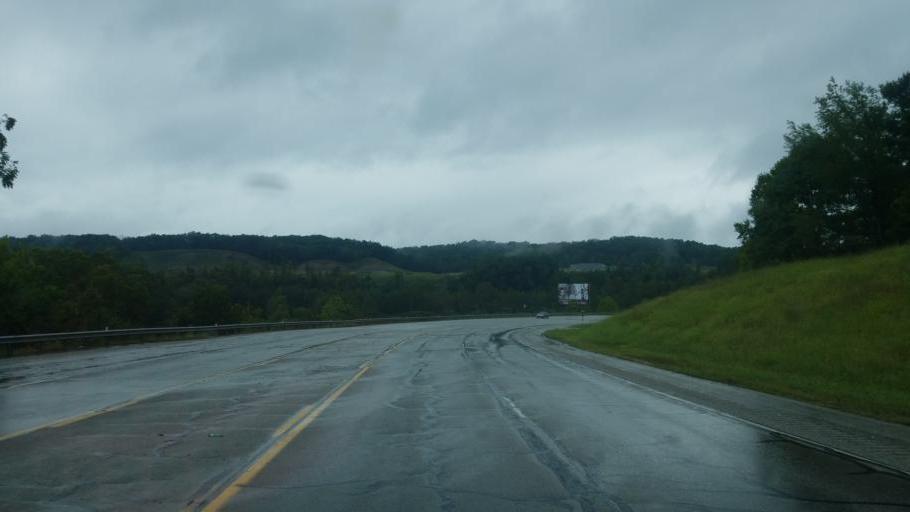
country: US
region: Kentucky
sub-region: Rowan County
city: Morehead
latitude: 38.1950
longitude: -83.4811
